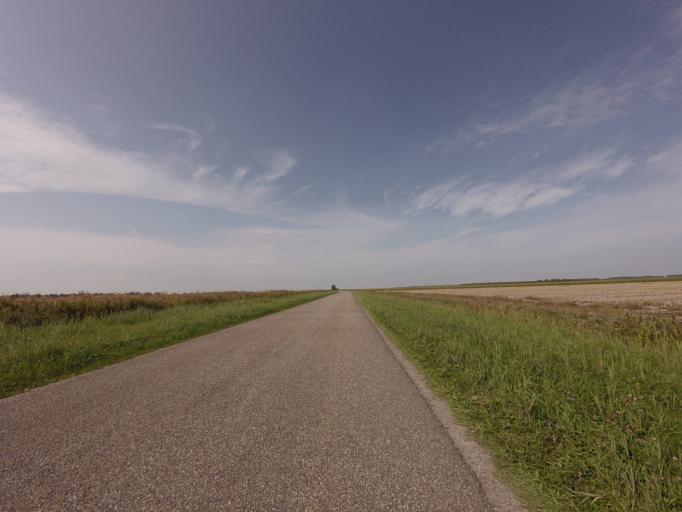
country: NL
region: Groningen
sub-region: Gemeente De Marne
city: Ulrum
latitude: 53.3443
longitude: 6.2789
